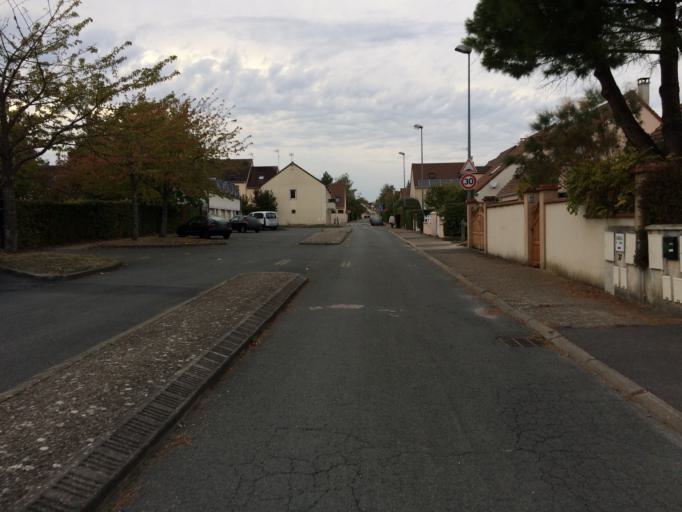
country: FR
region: Ile-de-France
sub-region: Departement de l'Essonne
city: Marcoussis
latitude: 48.6387
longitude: 2.2380
